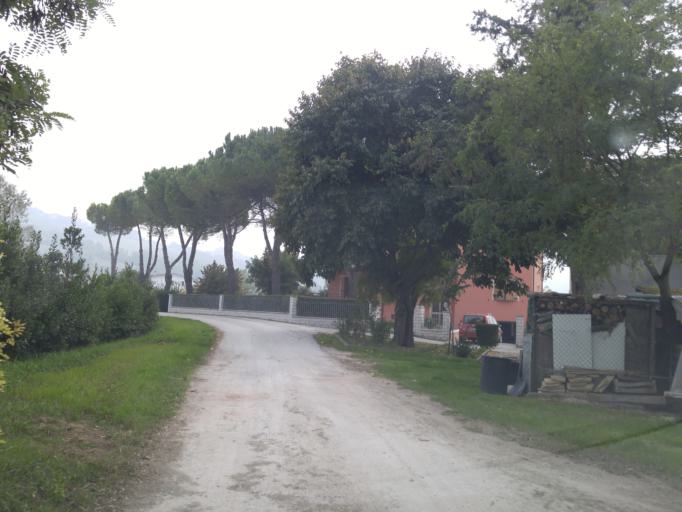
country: IT
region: The Marches
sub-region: Provincia di Pesaro e Urbino
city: Villanova
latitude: 43.7355
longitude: 12.9215
